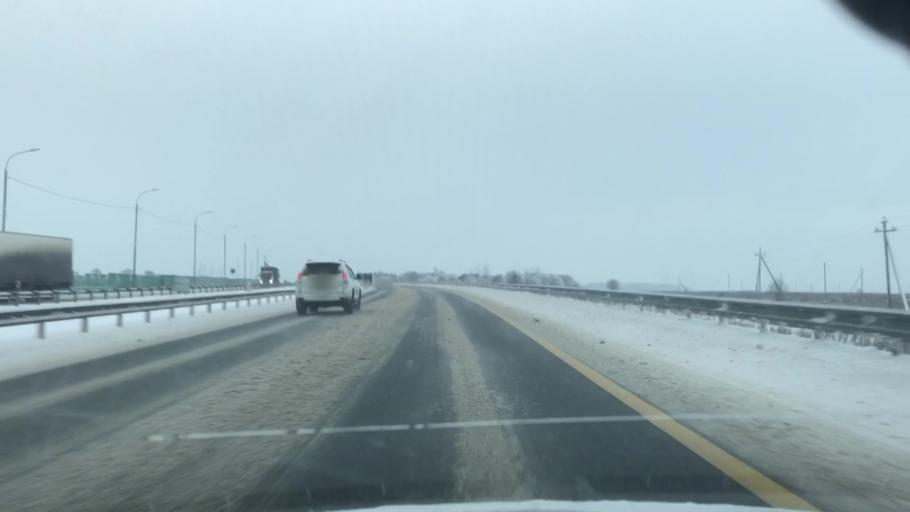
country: RU
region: Moskovskaya
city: Mikhnevo
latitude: 55.1175
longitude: 37.9275
